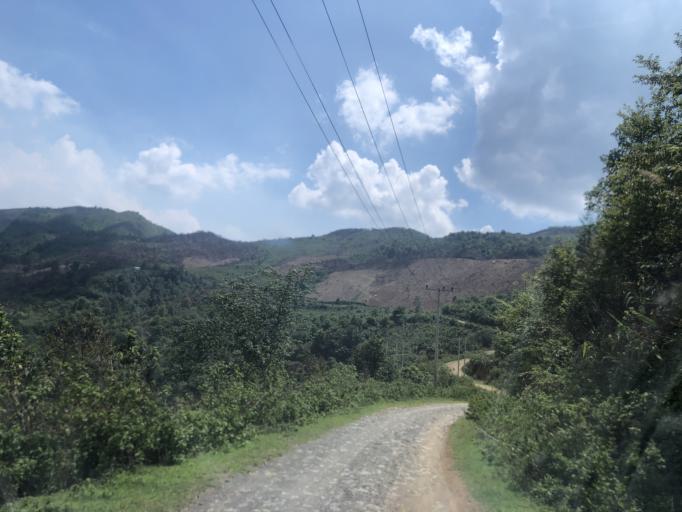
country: LA
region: Phongsali
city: Phongsali
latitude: 21.3969
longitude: 102.2242
